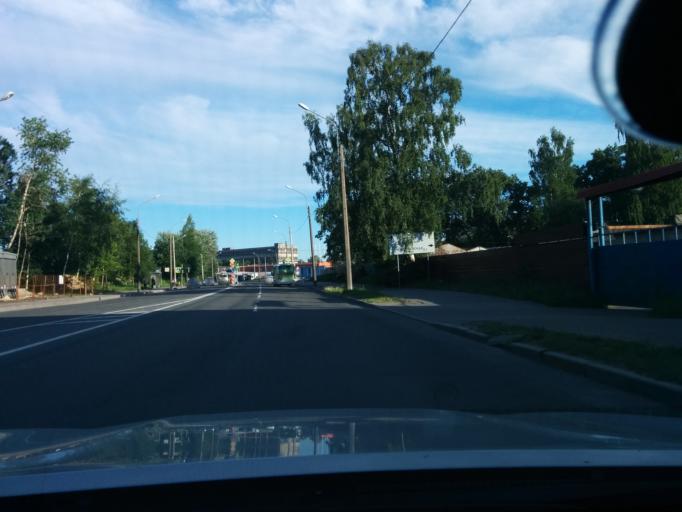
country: RU
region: Leningrad
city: Finlyandskiy
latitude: 59.9788
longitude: 30.3668
